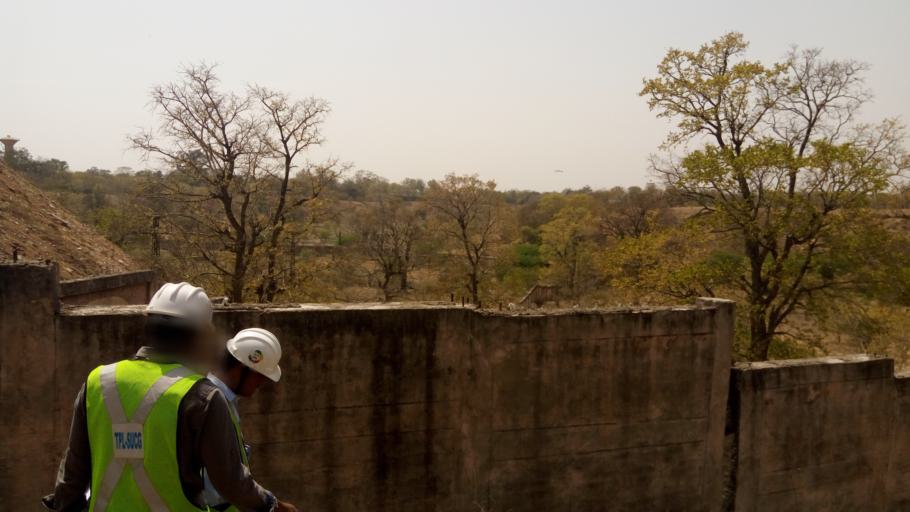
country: IN
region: Rajasthan
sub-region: Jaipur
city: Jaipur
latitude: 26.9382
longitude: 75.7848
